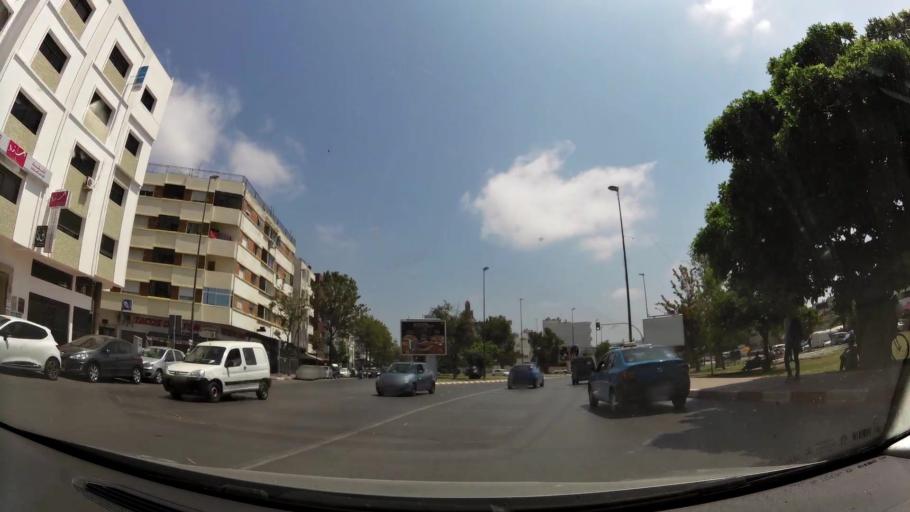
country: MA
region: Rabat-Sale-Zemmour-Zaer
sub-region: Rabat
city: Rabat
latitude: 34.0029
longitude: -6.8514
